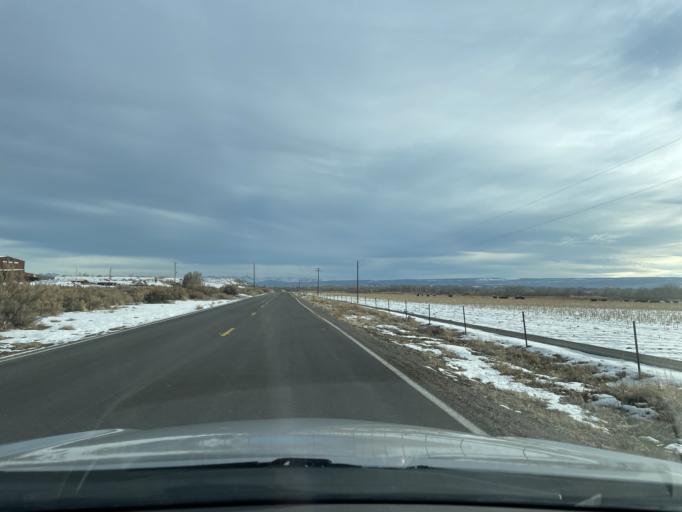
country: US
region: Colorado
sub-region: Montrose County
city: Olathe
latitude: 38.6586
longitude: -107.9977
